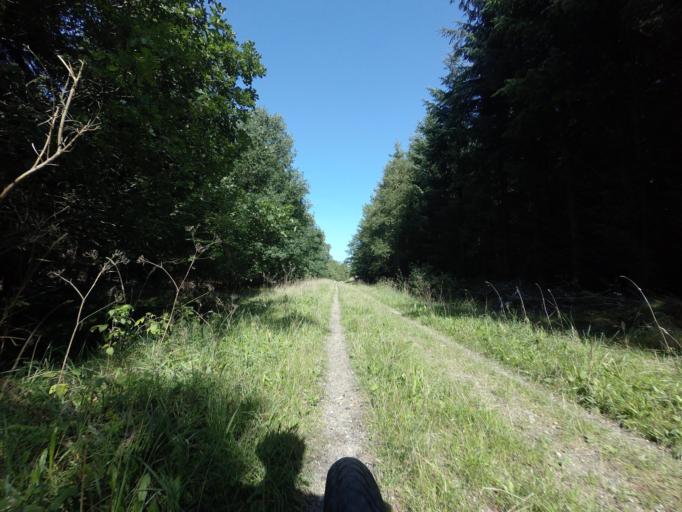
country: DK
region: North Denmark
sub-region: Hjorring Kommune
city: Hirtshals
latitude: 57.5786
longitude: 10.0022
